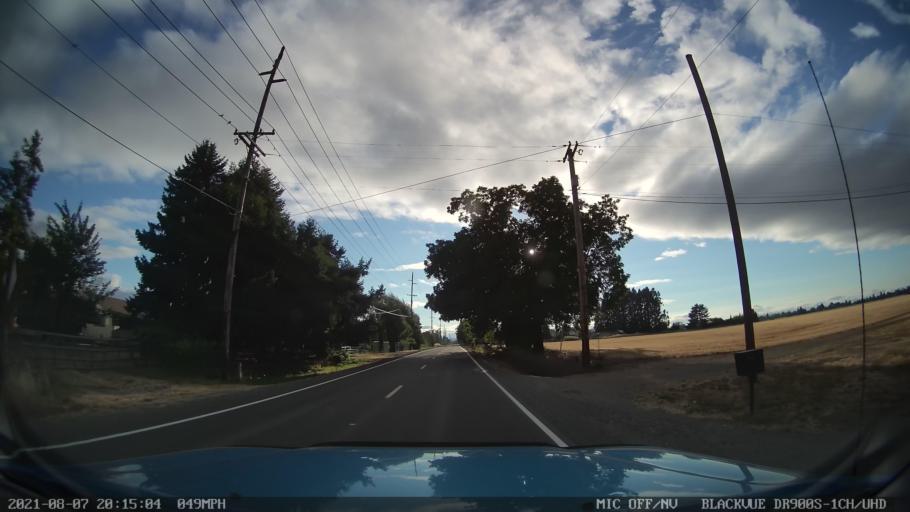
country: US
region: Oregon
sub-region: Marion County
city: Four Corners
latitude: 44.9548
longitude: -122.9500
